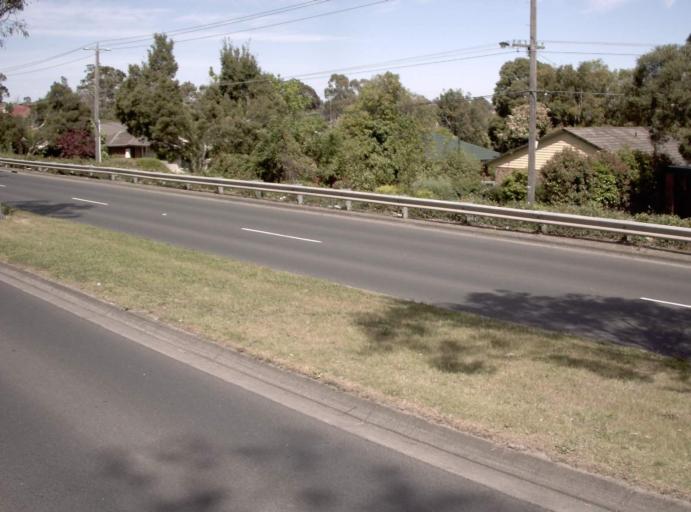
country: AU
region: Victoria
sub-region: Manningham
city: Donvale
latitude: -37.7793
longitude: 145.1638
